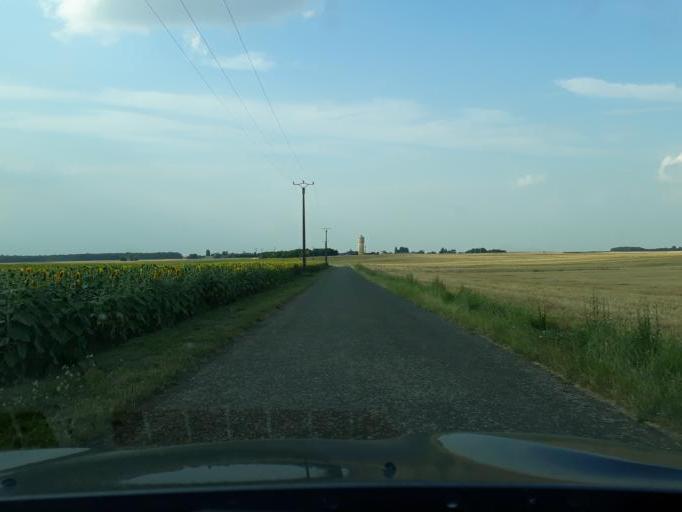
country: FR
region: Centre
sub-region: Departement du Loir-et-Cher
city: Mer
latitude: 47.8071
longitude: 1.4937
